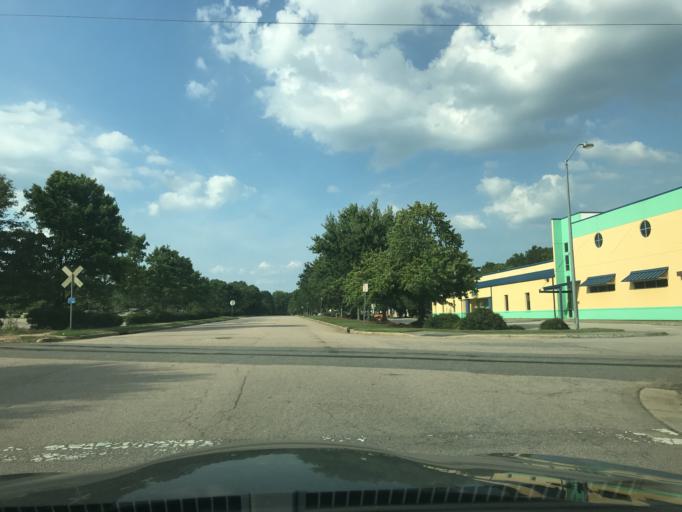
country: US
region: North Carolina
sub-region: Wake County
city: Raleigh
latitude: 35.8555
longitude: -78.5987
